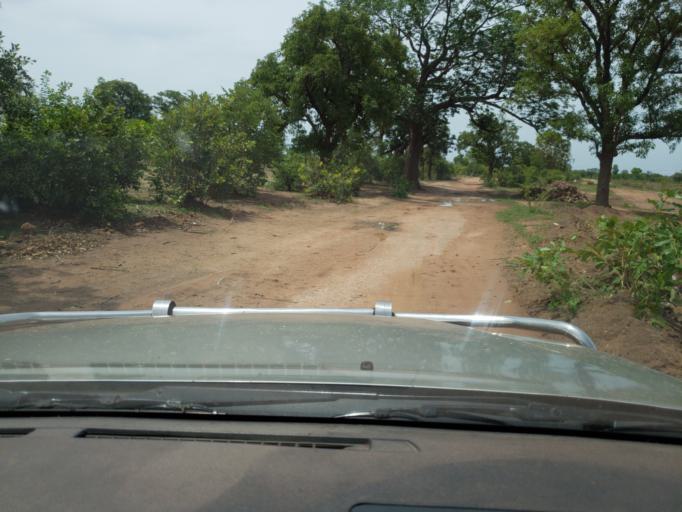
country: ML
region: Koulikoro
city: Kolokani
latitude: 13.4889
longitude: -8.2437
